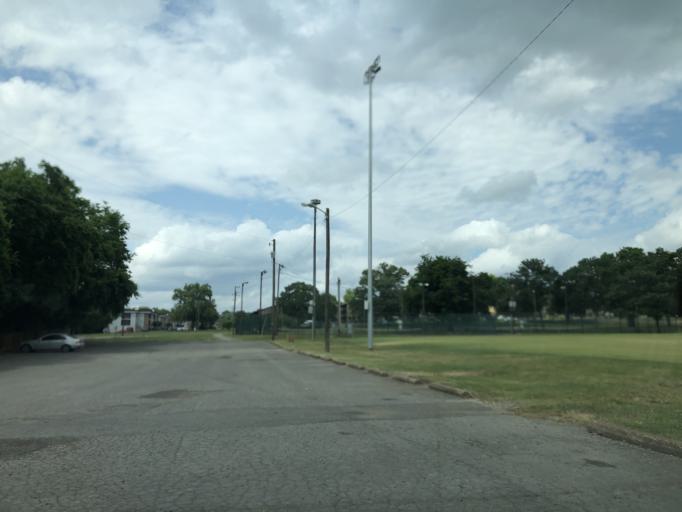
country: US
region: Tennessee
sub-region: Davidson County
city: Goodlettsville
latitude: 36.2659
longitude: -86.7024
